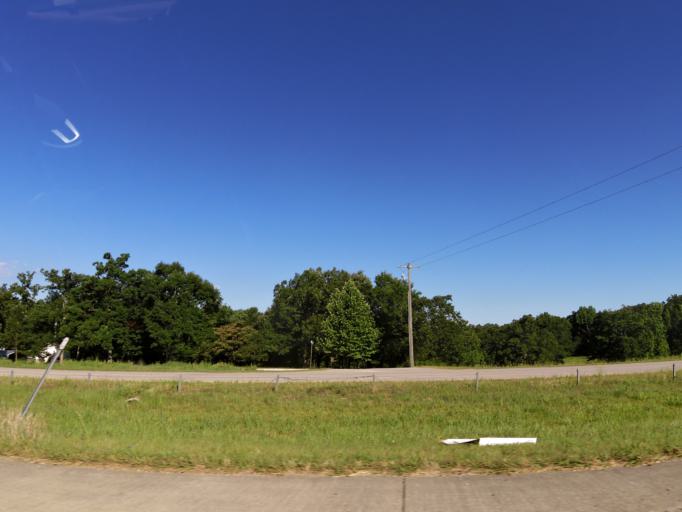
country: US
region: Missouri
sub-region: Butler County
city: Poplar Bluff
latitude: 36.7050
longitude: -90.4719
